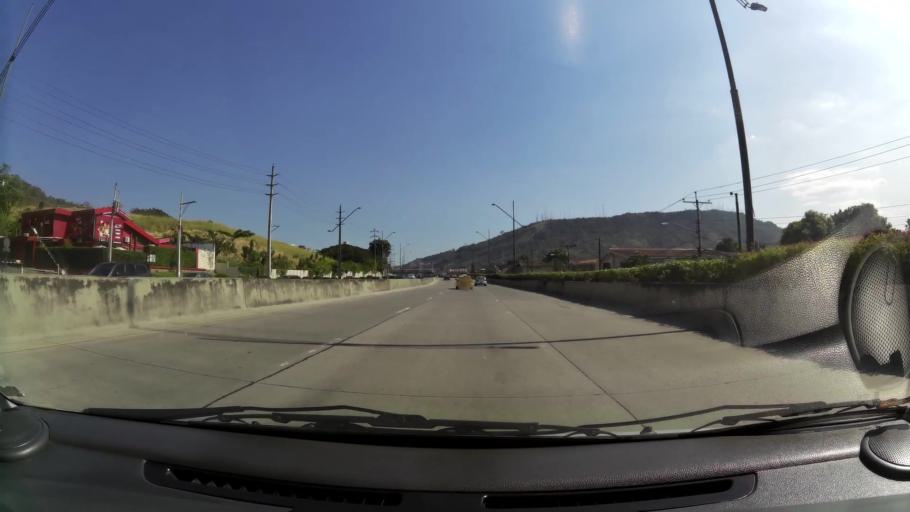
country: EC
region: Guayas
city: Guayaquil
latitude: -2.1638
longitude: -79.9318
